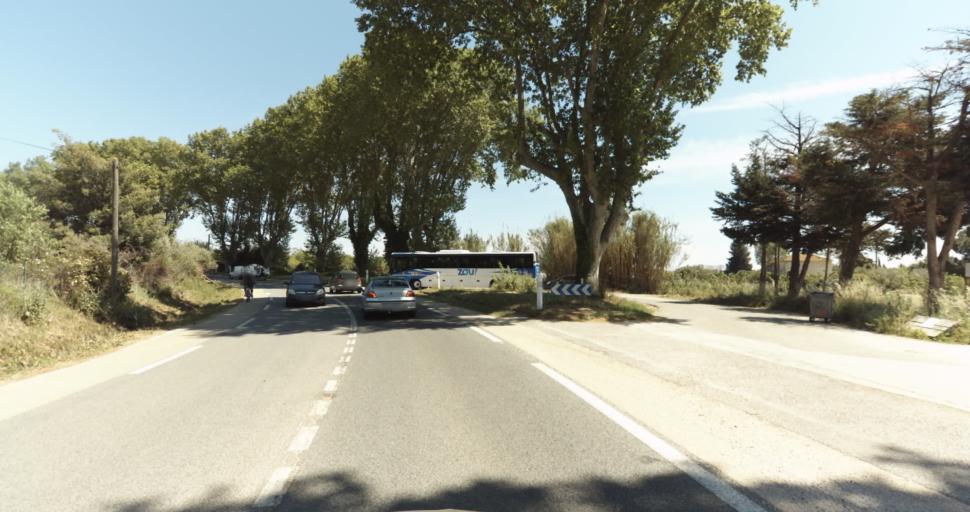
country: FR
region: Provence-Alpes-Cote d'Azur
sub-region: Departement du Var
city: Hyeres
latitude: 43.1303
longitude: 6.1680
